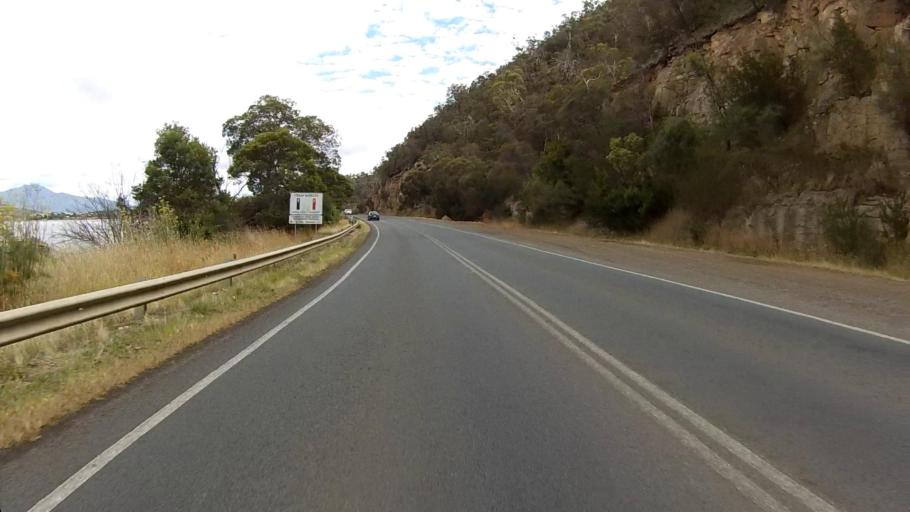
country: AU
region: Tasmania
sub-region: Brighton
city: Old Beach
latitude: -42.7896
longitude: 147.2929
